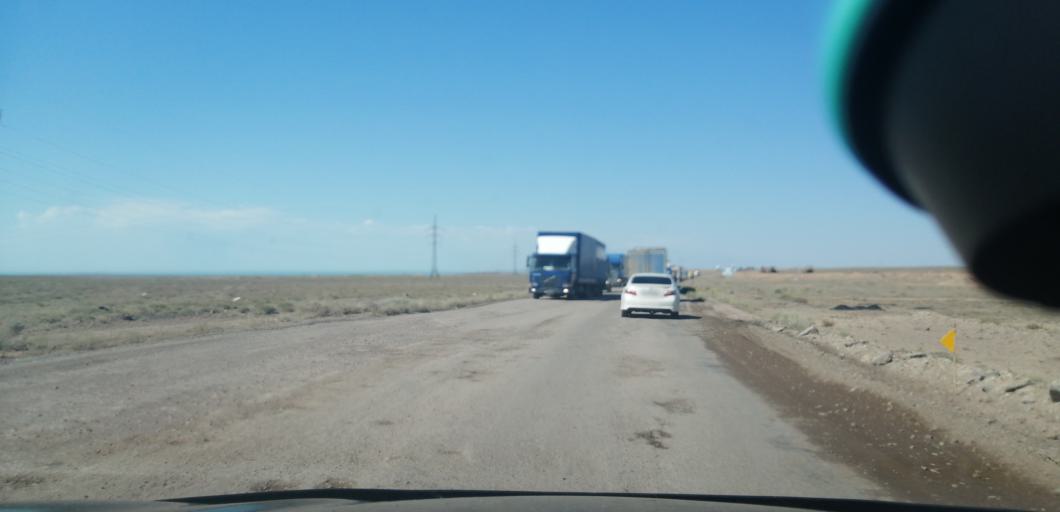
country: KZ
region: Qaraghandy
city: Balqash
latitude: 46.8238
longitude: 74.7748
